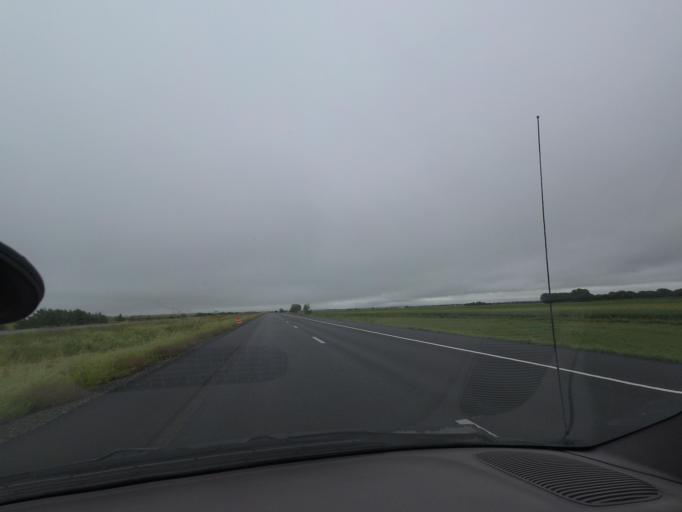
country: US
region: Illinois
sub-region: Macon County
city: Harristown
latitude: 39.8311
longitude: -89.1369
